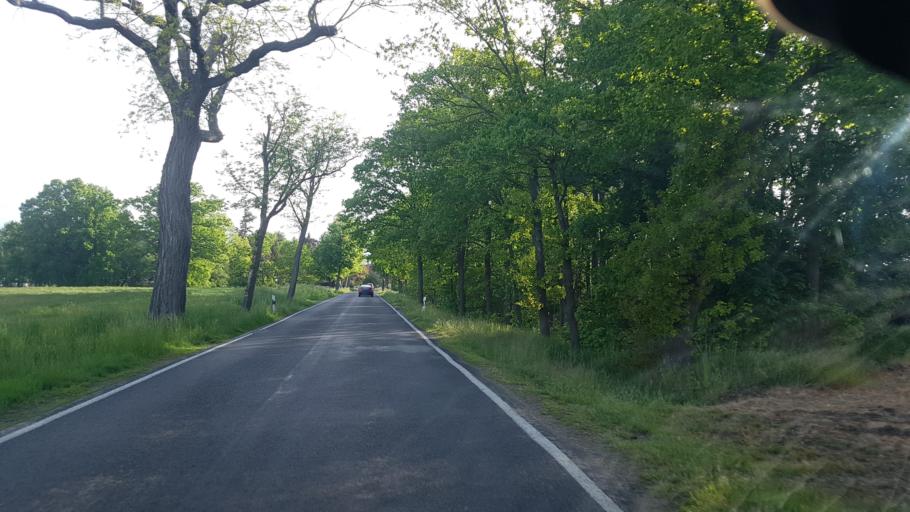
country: DE
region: Brandenburg
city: Dahme
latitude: 51.8832
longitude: 13.4542
